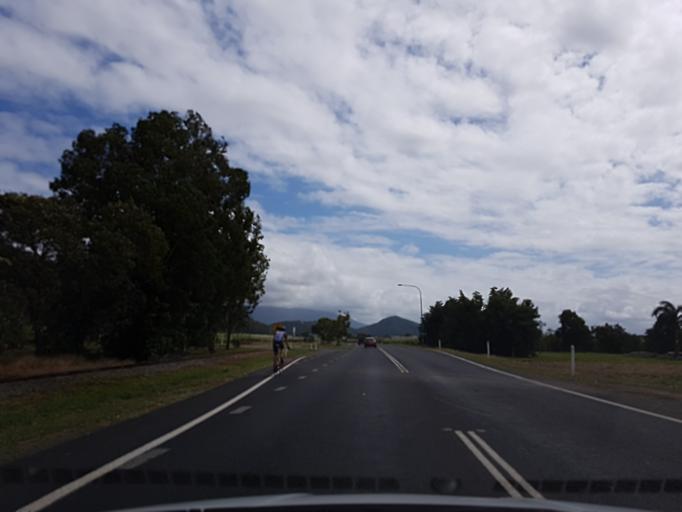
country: AU
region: Queensland
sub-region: Cairns
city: Port Douglas
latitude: -16.4928
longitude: 145.4224
